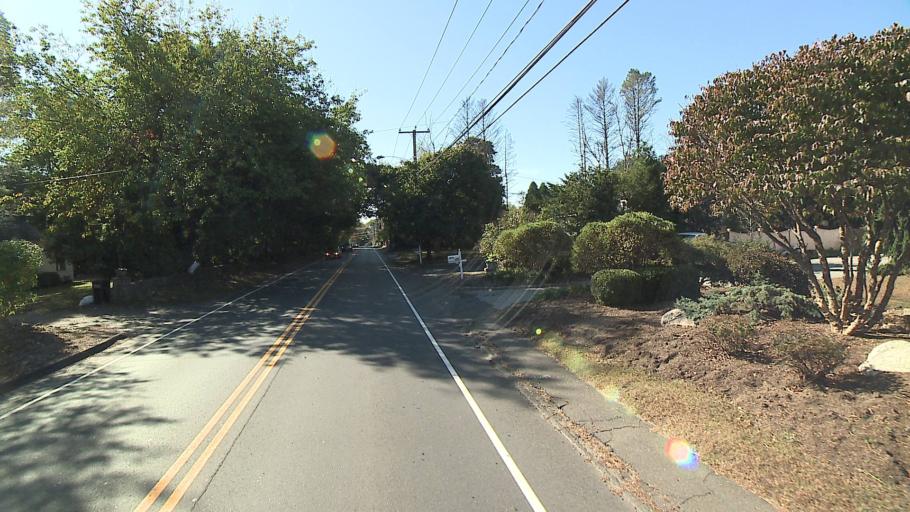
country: US
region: Connecticut
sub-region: Fairfield County
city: Westport
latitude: 41.1599
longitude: -73.3577
